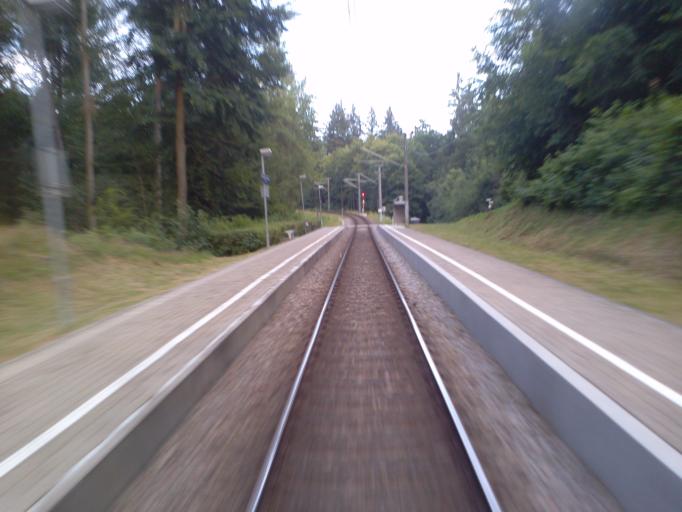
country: DE
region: Baden-Wuerttemberg
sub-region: Karlsruhe Region
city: Ettlingen
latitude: 48.9192
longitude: 8.4727
